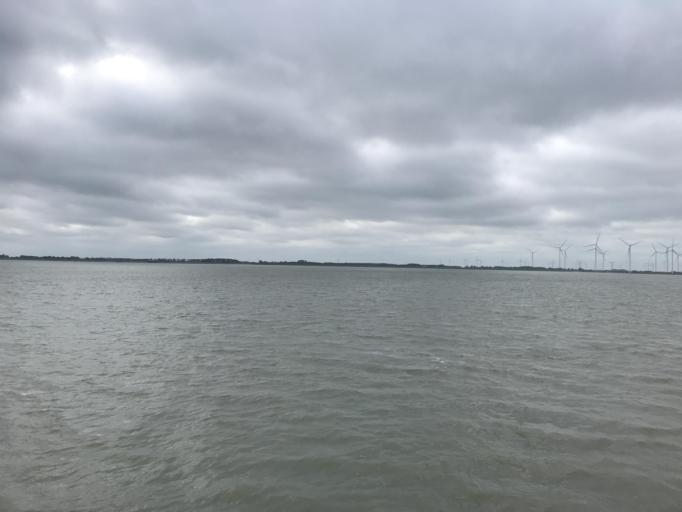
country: NL
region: Groningen
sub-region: Gemeente Delfzijl
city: Delfzijl
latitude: 53.3248
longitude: 7.0376
